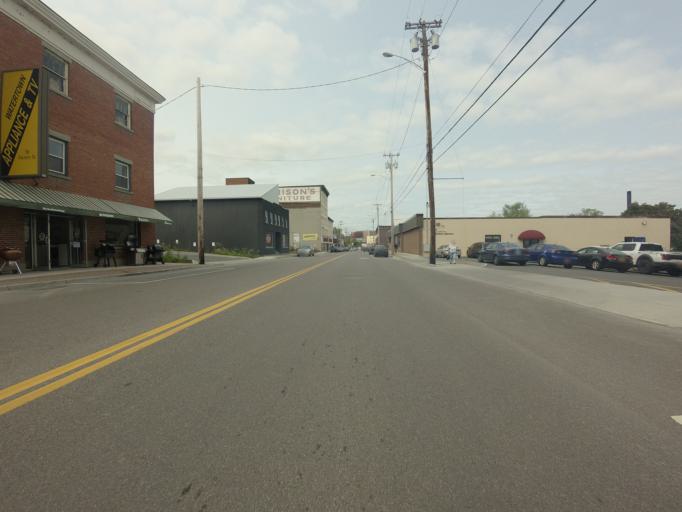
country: US
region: New York
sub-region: Jefferson County
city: Watertown
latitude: 43.9760
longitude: -75.9045
